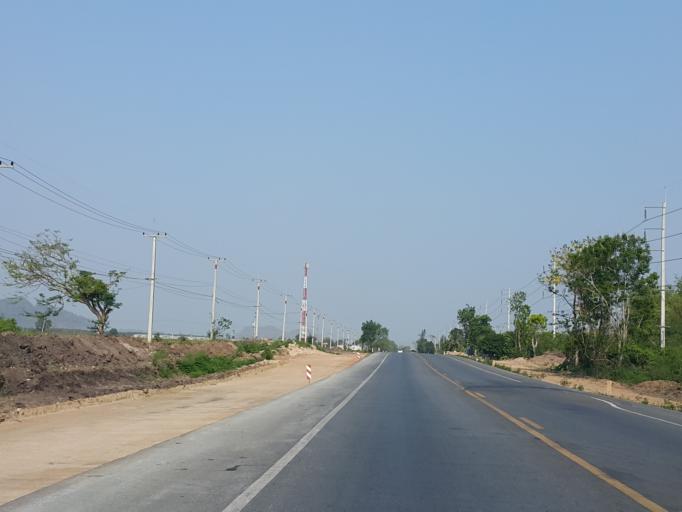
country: TH
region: Kanchanaburi
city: Sai Yok
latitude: 14.0882
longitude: 99.3294
